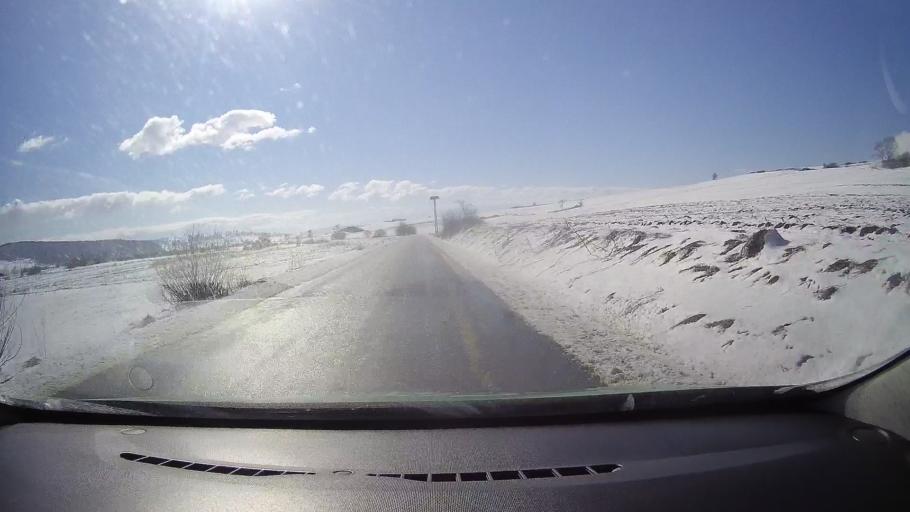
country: RO
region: Sibiu
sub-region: Comuna Vurpar
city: Vurpar
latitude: 45.8738
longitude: 24.3185
